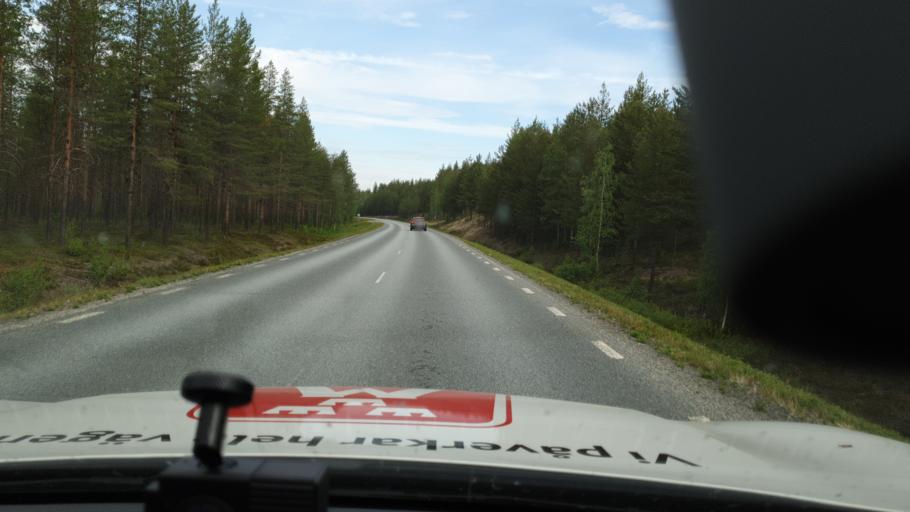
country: SE
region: Vaesterbotten
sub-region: Mala Kommun
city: Mala
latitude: 65.0067
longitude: 18.4632
